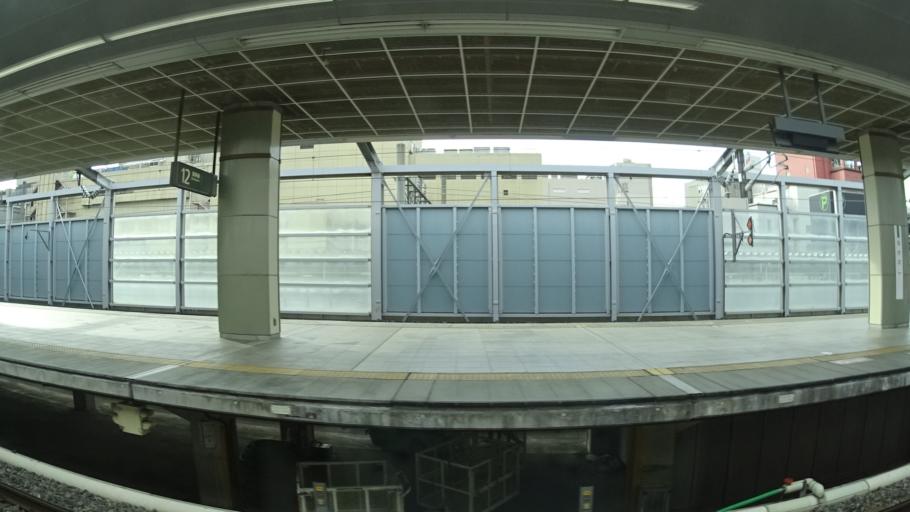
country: JP
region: Nagano
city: Nagano-shi
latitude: 36.6437
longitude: 138.1903
